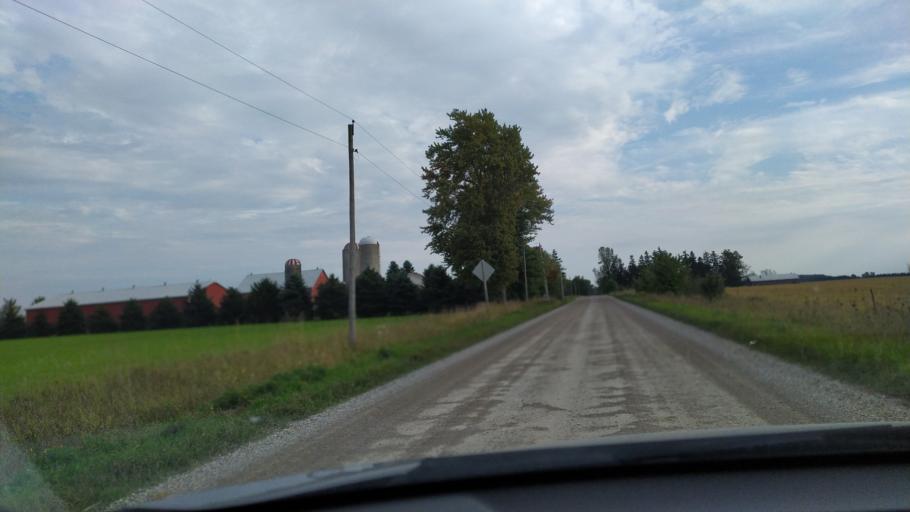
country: CA
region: Ontario
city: Stratford
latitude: 43.4229
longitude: -80.9132
